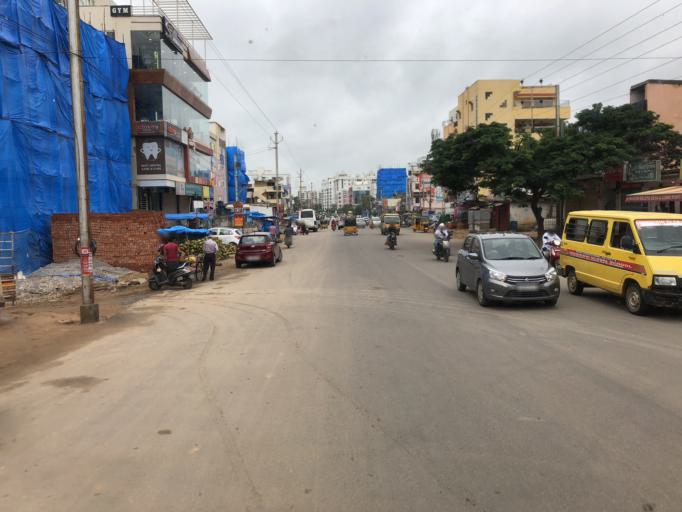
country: IN
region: Telangana
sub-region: Medak
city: Serilingampalle
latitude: 17.4605
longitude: 78.3541
